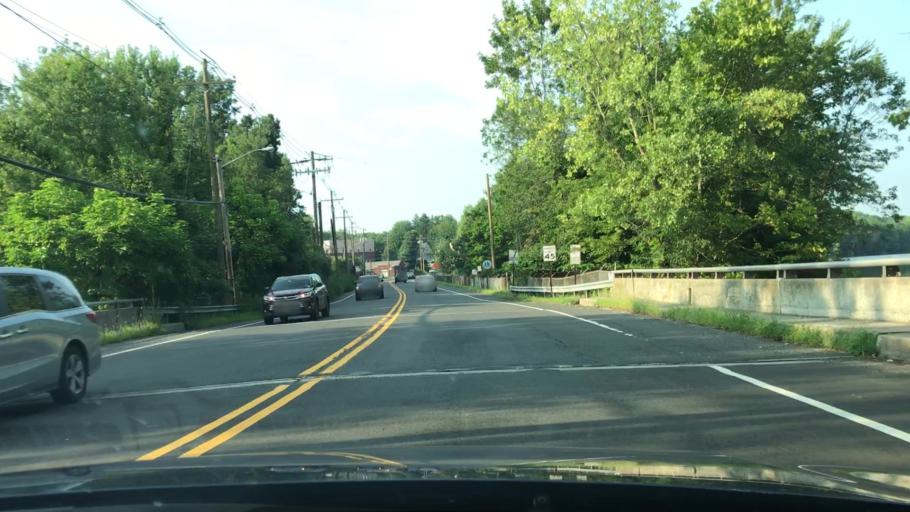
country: US
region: New Jersey
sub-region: Bergen County
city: Harrington Park
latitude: 40.9797
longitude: -73.9790
